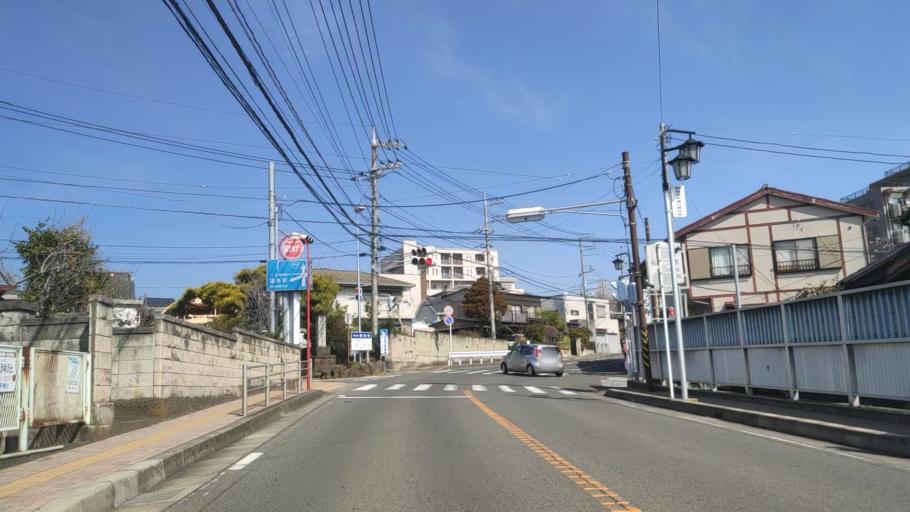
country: JP
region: Kanagawa
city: Isehara
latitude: 35.3841
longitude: 139.2793
